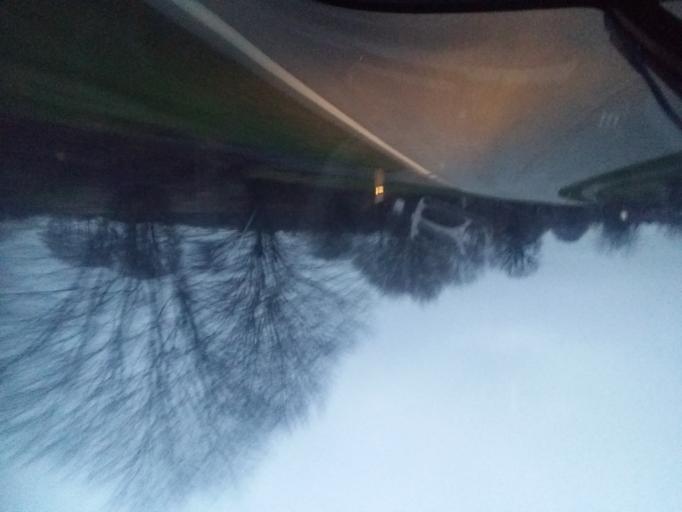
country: DE
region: Schleswig-Holstein
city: Warringholz
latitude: 54.0781
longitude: 9.4628
